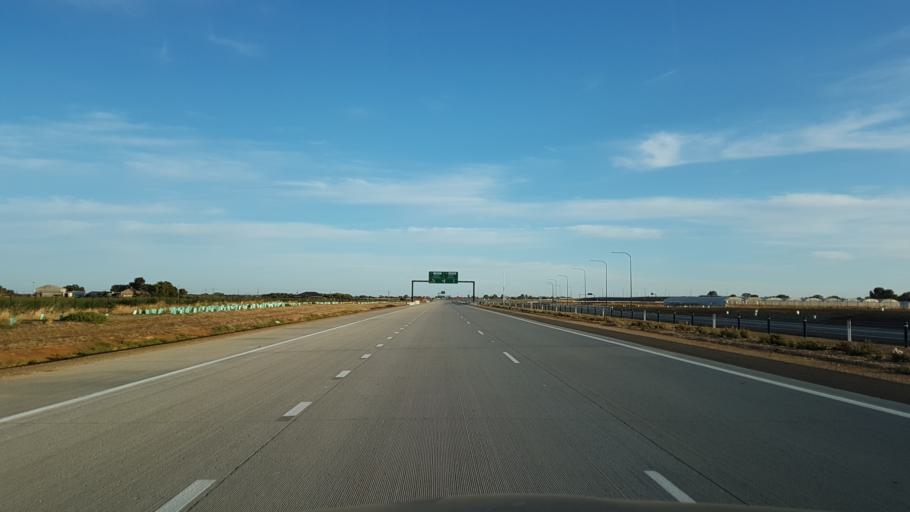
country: AU
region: South Australia
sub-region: Playford
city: Virginia
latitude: -34.7179
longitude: 138.5725
